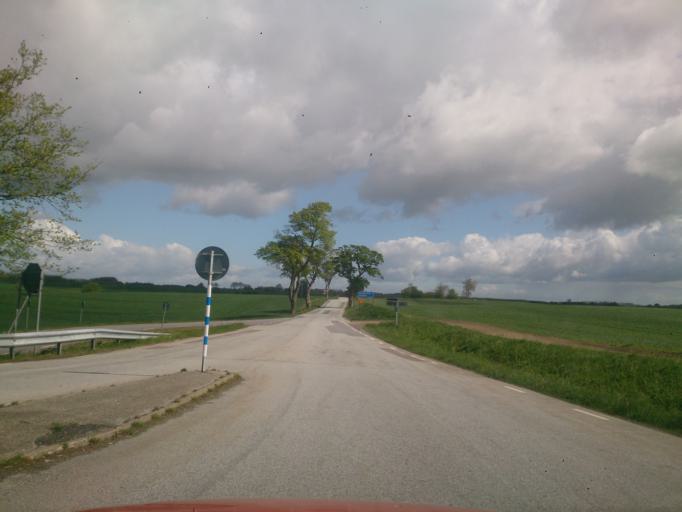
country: SE
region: Skane
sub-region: Ystads Kommun
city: Ystad
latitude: 55.4688
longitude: 13.7071
